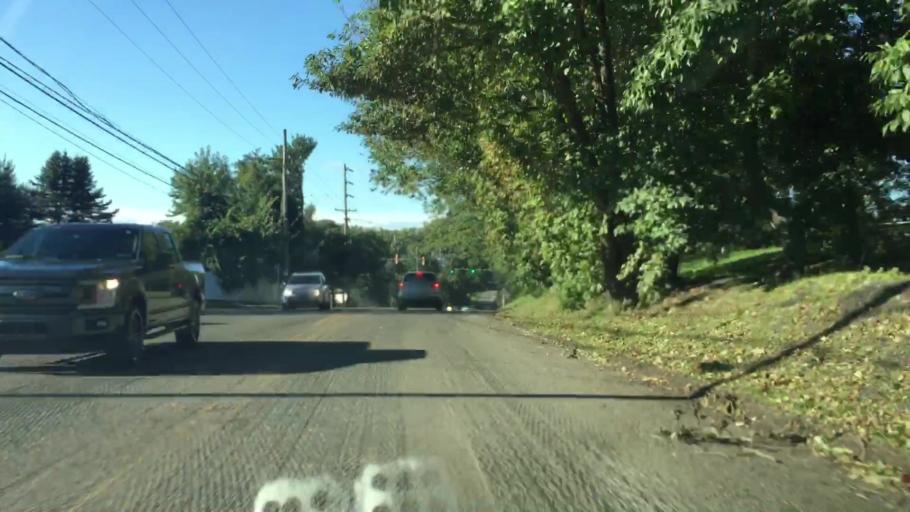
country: US
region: Pennsylvania
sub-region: Delaware County
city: Boothwyn
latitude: 39.8485
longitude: -75.4506
